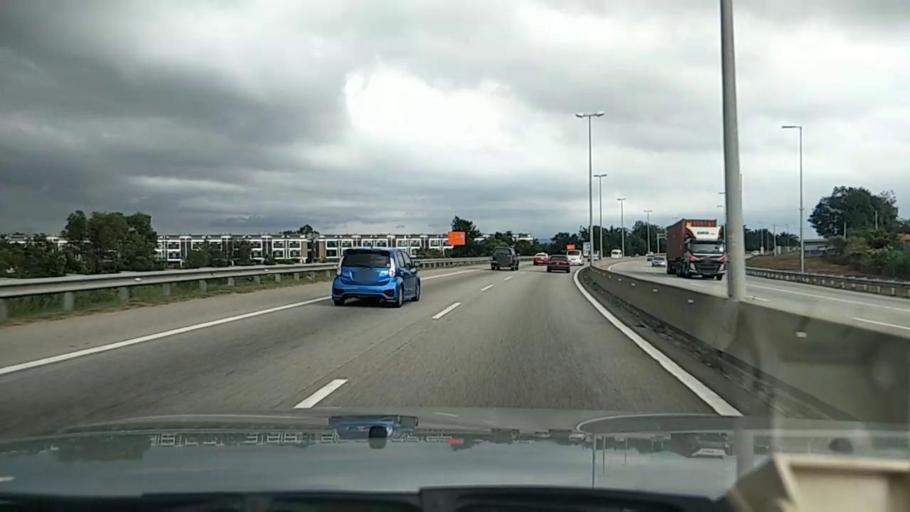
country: MY
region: Putrajaya
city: Putrajaya
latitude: 2.9370
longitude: 101.6262
